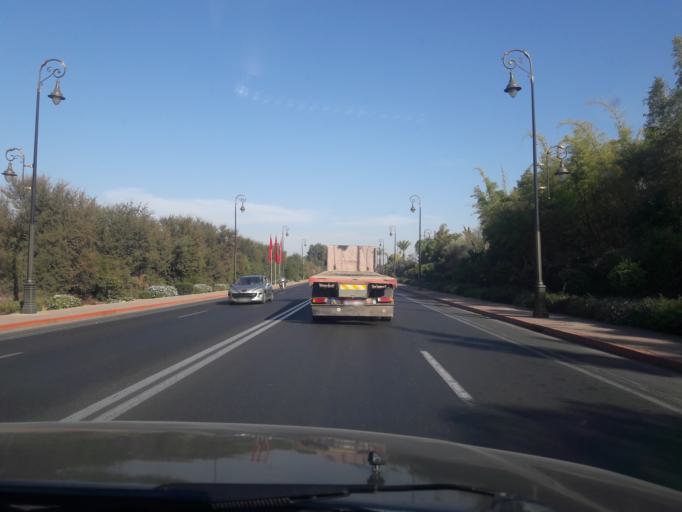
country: MA
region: Marrakech-Tensift-Al Haouz
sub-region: Marrakech
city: Marrakesh
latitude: 31.6471
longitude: -7.9710
